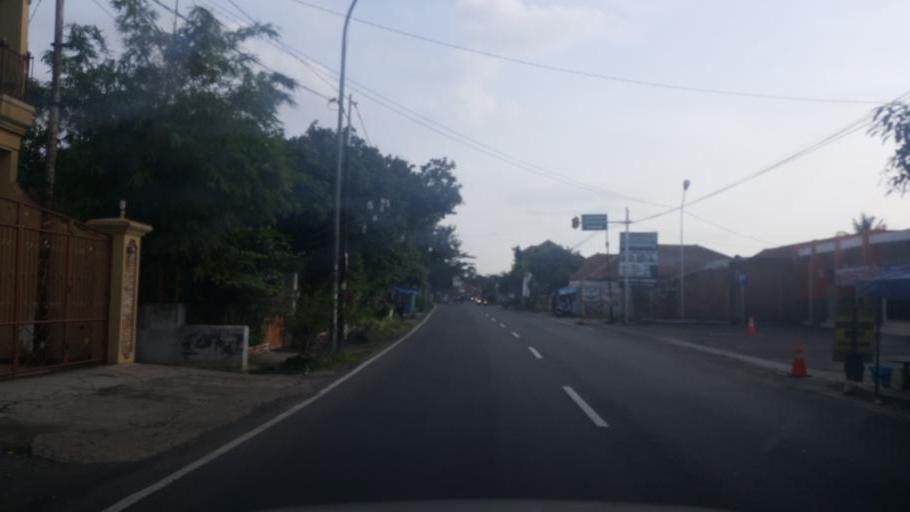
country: ID
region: West Java
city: Cibogor
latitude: -7.3148
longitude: 108.2285
